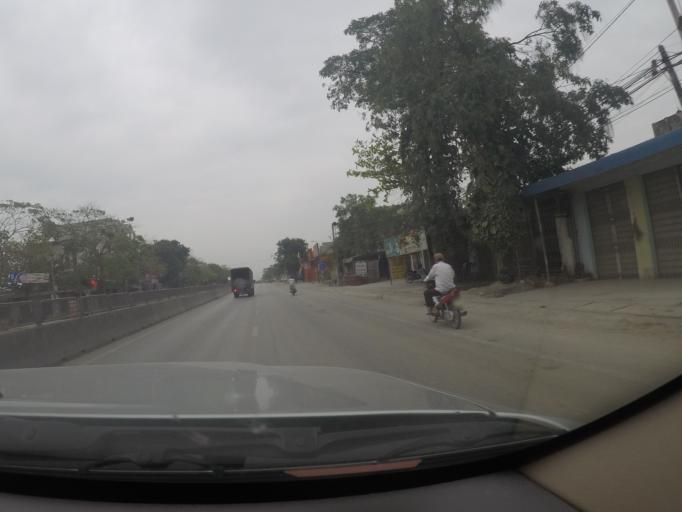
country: VN
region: Nghe An
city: Dien Chau
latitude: 19.0455
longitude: 105.5826
